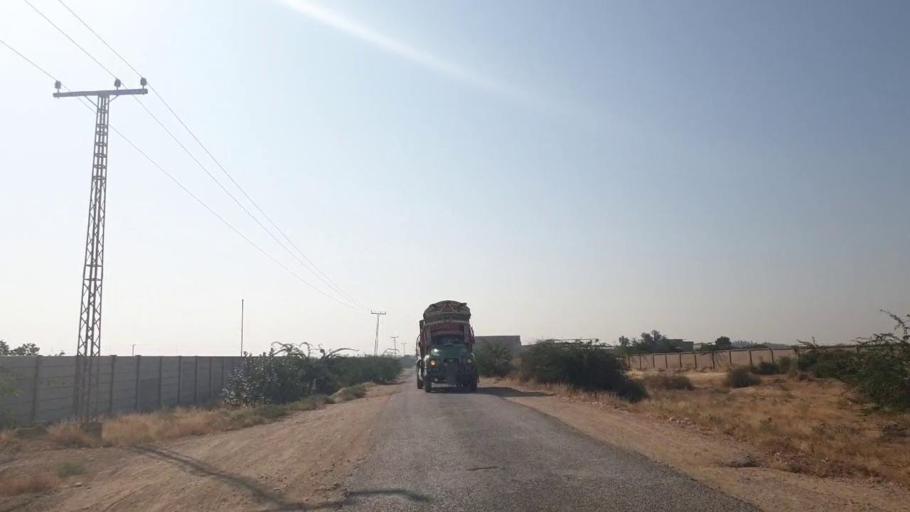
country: PK
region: Sindh
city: Thatta
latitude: 25.1588
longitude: 67.7734
